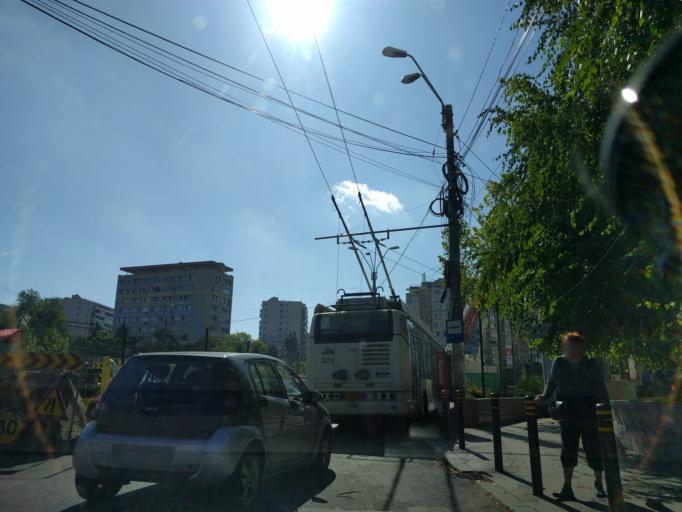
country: RO
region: Bucuresti
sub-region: Municipiul Bucuresti
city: Bucharest
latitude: 44.4249
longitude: 26.1369
